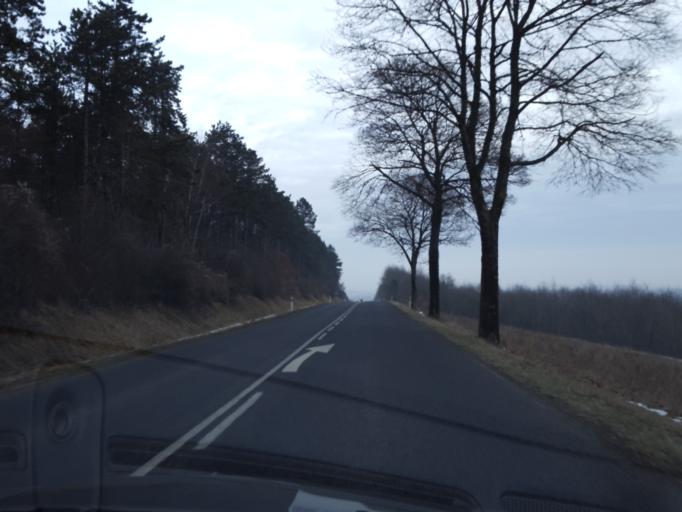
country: FR
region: Lorraine
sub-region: Departement de la Meuse
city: Verdun
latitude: 49.1802
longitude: 5.4840
